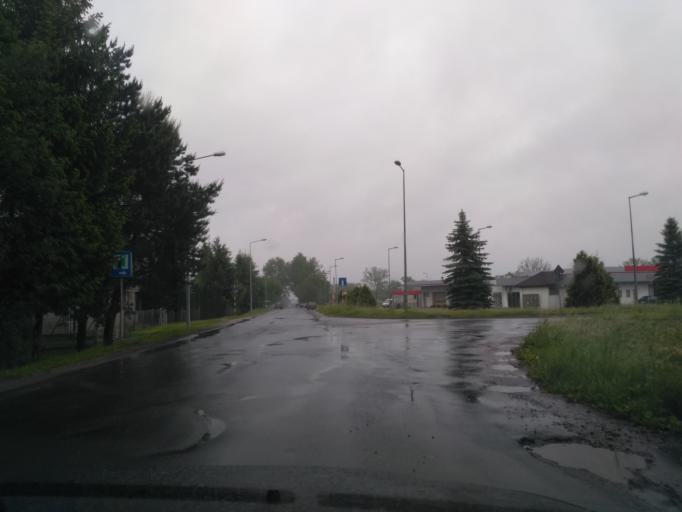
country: PL
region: Lesser Poland Voivodeship
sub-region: Powiat gorlicki
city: Kobylanka
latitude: 49.6844
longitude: 21.1882
